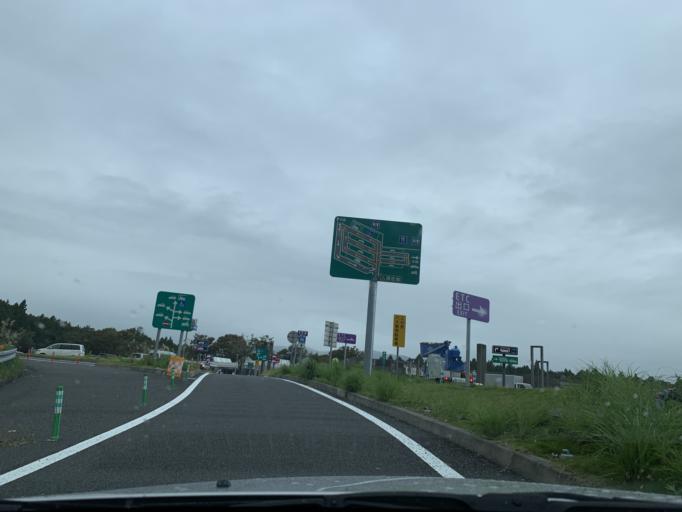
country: JP
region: Shizuoka
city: Gotemba
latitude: 35.3133
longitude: 138.9639
